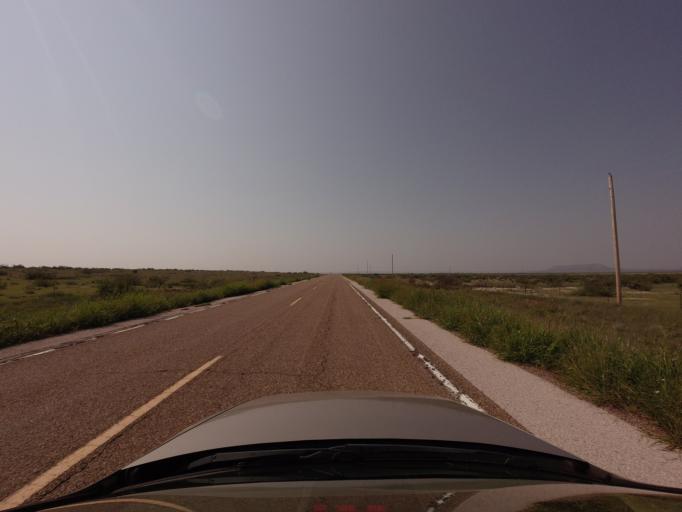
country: US
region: New Mexico
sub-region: Quay County
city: Tucumcari
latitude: 34.9930
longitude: -103.7462
